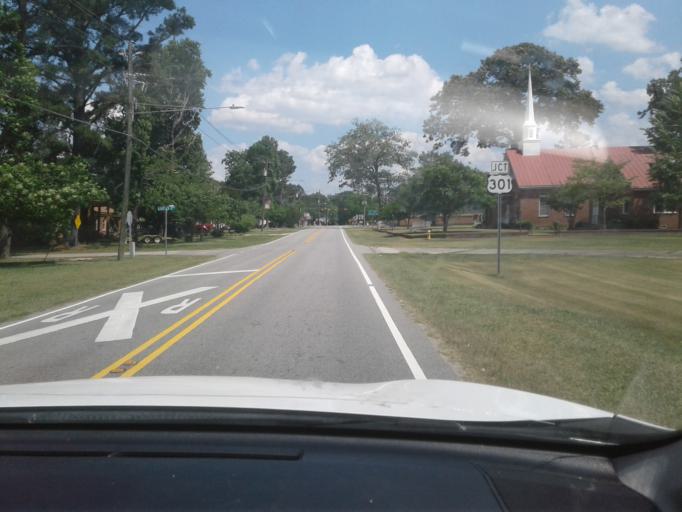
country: US
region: North Carolina
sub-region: Harnett County
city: Erwin
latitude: 35.2173
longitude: -78.6799
